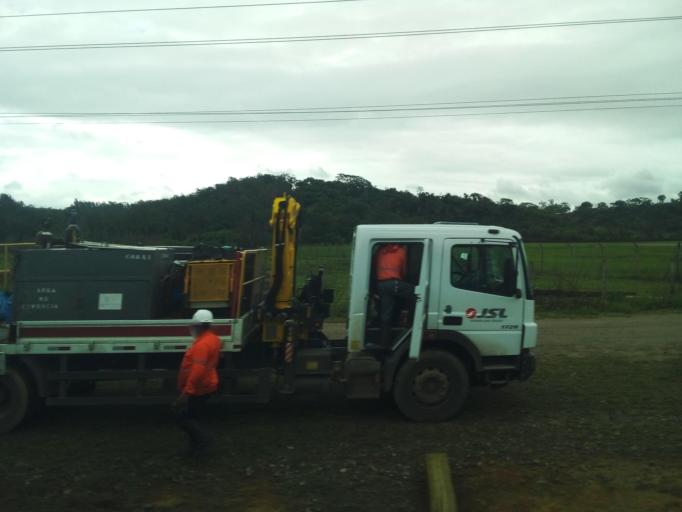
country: BR
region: Minas Gerais
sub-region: Ipatinga
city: Ipatinga
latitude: -19.4811
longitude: -42.4918
